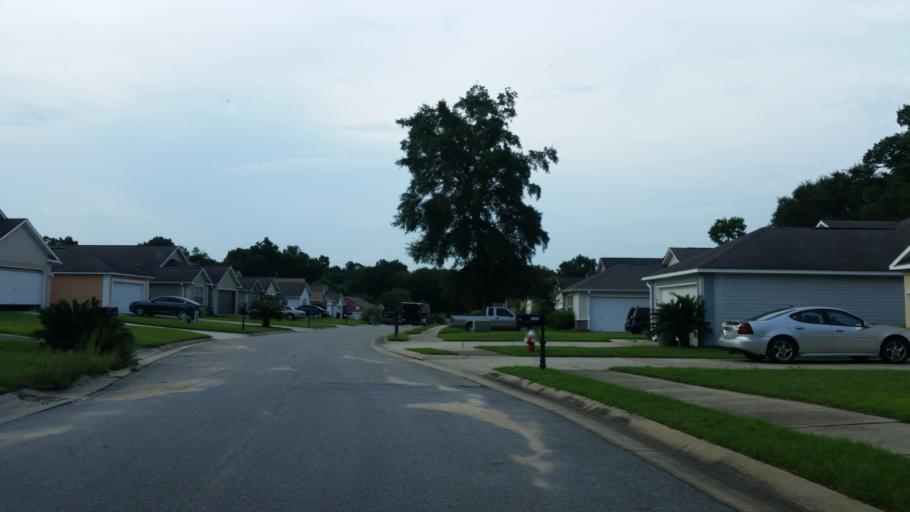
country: US
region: Florida
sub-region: Escambia County
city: Ferry Pass
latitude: 30.5119
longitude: -87.2006
